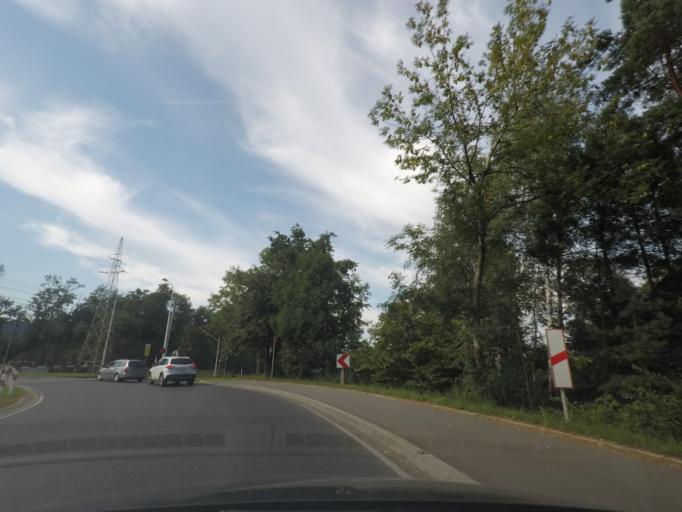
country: PL
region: Lesser Poland Voivodeship
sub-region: Powiat oswiecimski
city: Brzeszcze
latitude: 49.9745
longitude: 19.1296
